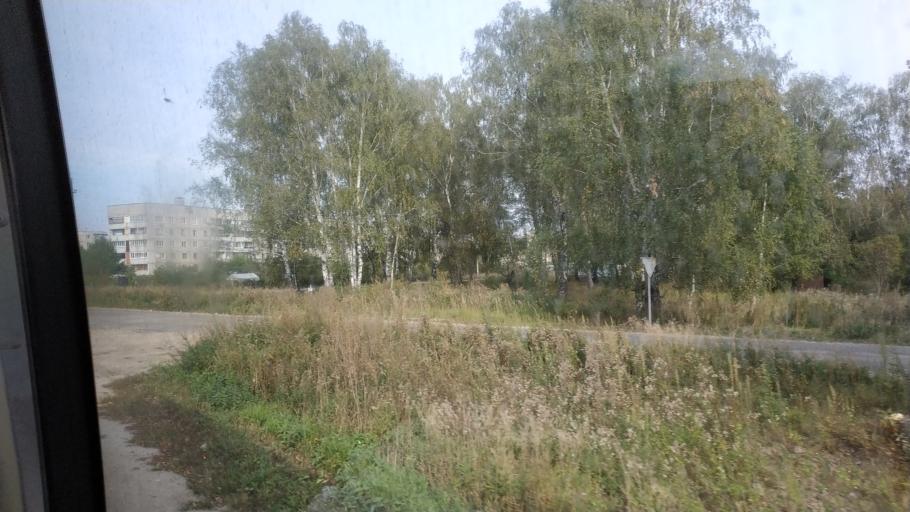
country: RU
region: Moskovskaya
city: Il'inskoye
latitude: 55.3339
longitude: 38.0881
